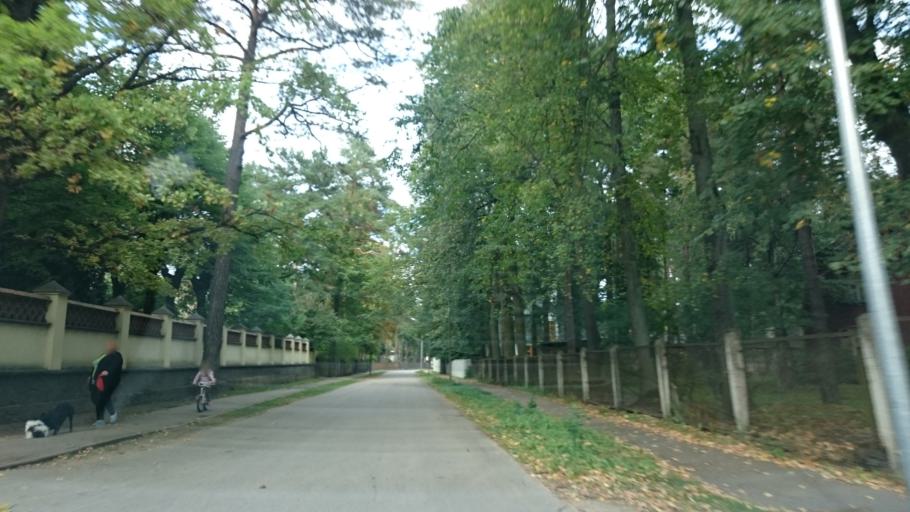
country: LV
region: Riga
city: Jaunciems
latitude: 56.9983
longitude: 24.1565
